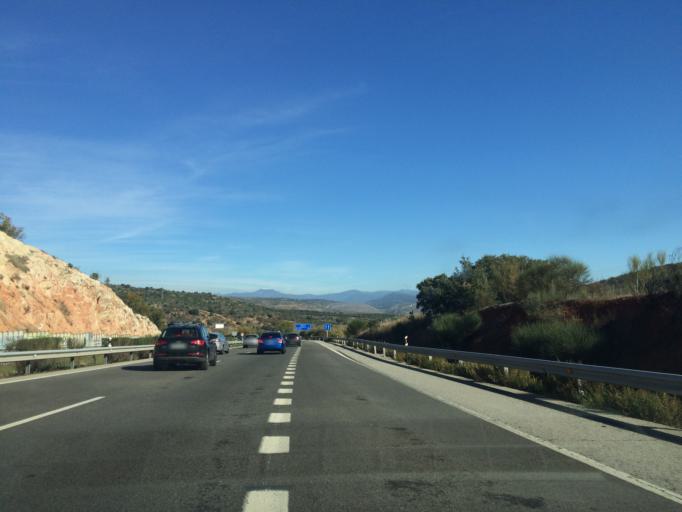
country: ES
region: Madrid
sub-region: Provincia de Madrid
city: Venturada
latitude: 40.7957
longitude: -3.6172
